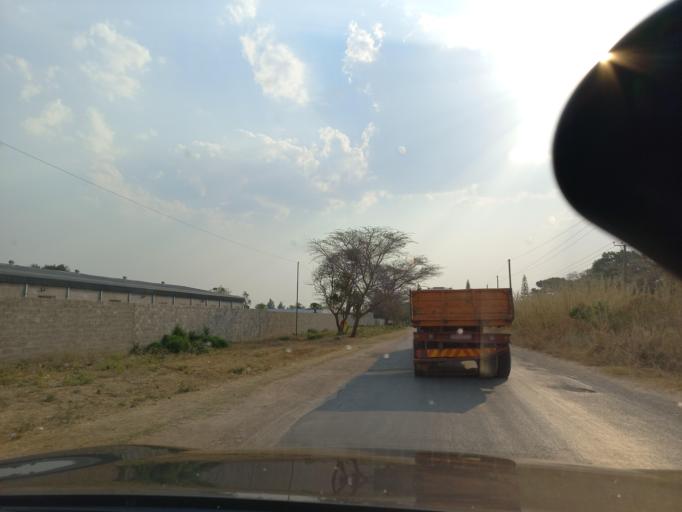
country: ZM
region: Lusaka
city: Lusaka
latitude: -15.4772
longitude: 28.2079
